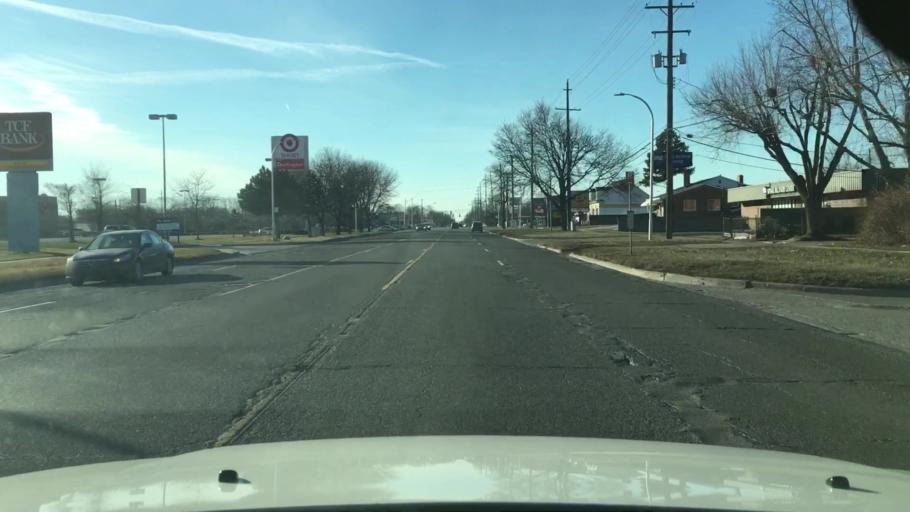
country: US
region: Michigan
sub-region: Oakland County
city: Madison Heights
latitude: 42.5054
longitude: -83.0810
